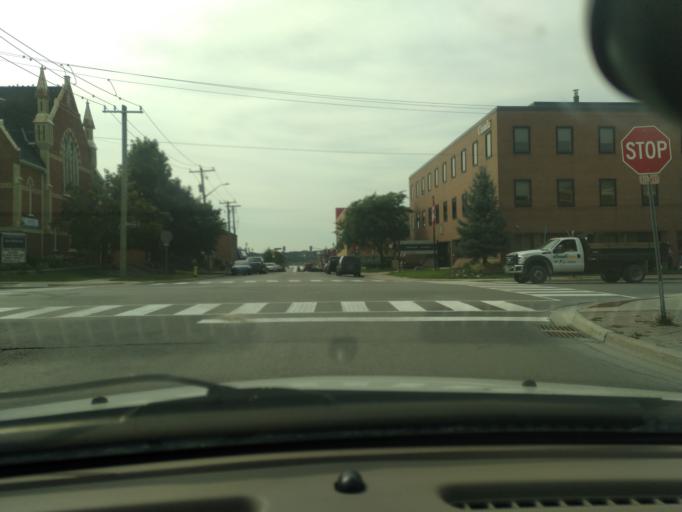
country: CA
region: Ontario
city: Barrie
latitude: 44.3917
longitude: -79.6880
